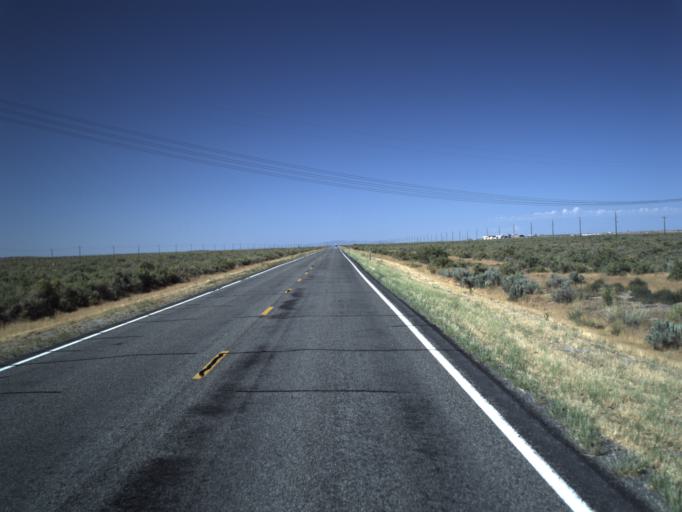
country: US
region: Utah
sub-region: Millard County
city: Delta
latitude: 39.4892
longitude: -112.4041
